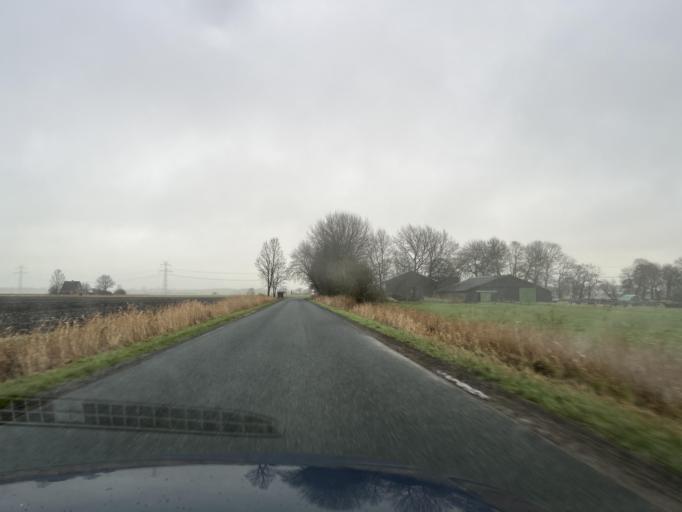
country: DE
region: Schleswig-Holstein
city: Lohe-Rickelshof
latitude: 54.2203
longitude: 9.0466
